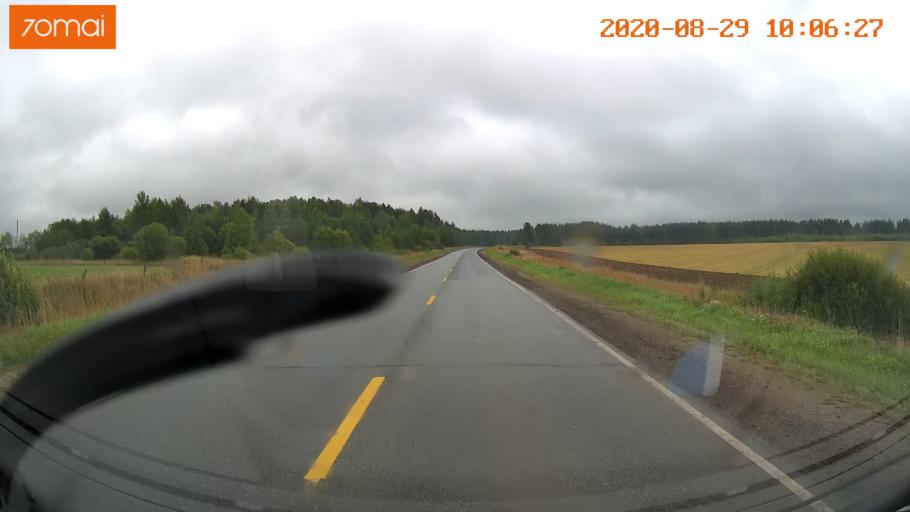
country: RU
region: Ivanovo
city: Kuznechikha
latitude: 57.3885
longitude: 42.5457
